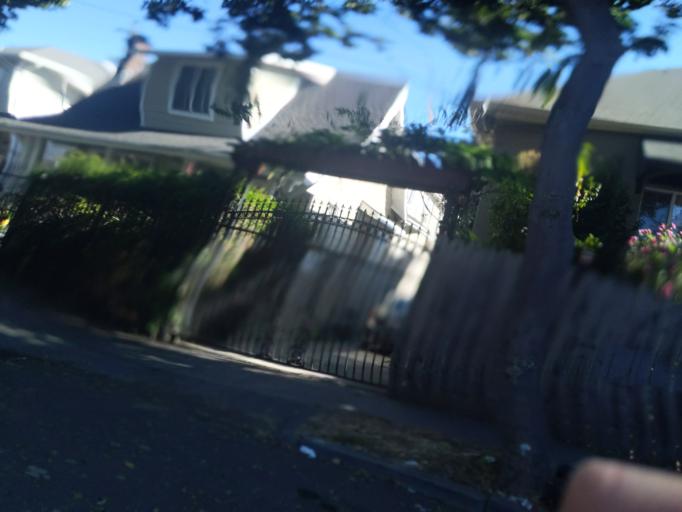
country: US
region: California
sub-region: Alameda County
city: Alameda
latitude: 37.7883
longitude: -122.2228
